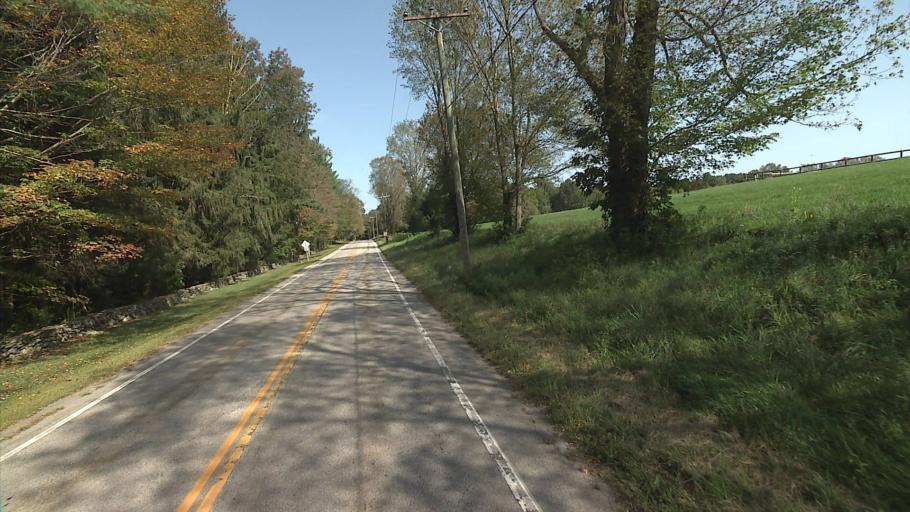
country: US
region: Connecticut
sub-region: Windham County
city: South Woodstock
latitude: 41.9133
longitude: -71.9559
